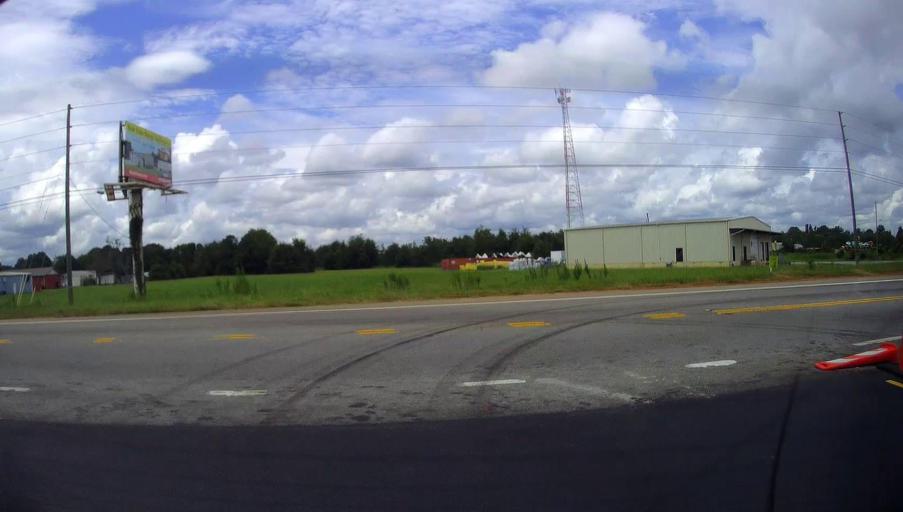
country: US
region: Georgia
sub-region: Peach County
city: Byron
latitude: 32.6091
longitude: -83.7484
